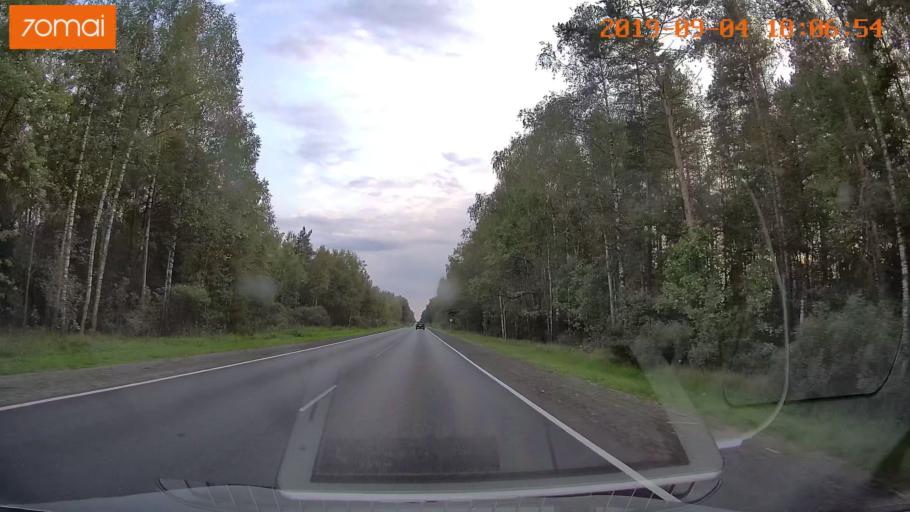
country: RU
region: Moskovskaya
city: Khorlovo
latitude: 55.4259
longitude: 38.8087
